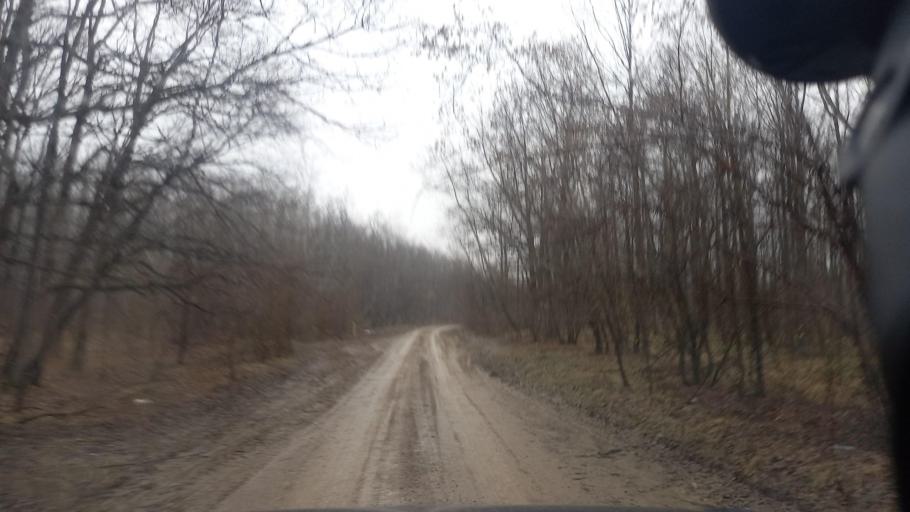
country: RU
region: Krasnodarskiy
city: Saratovskaya
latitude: 44.6513
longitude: 39.2434
